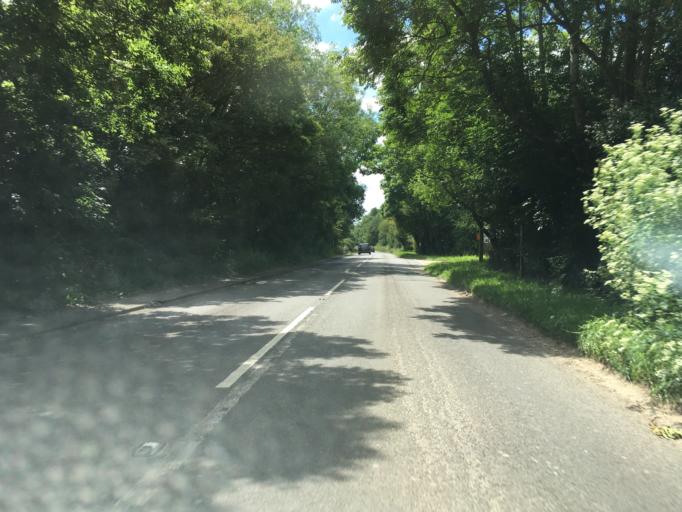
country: GB
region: England
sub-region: Hampshire
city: Colden Common
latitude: 50.9922
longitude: -1.3330
